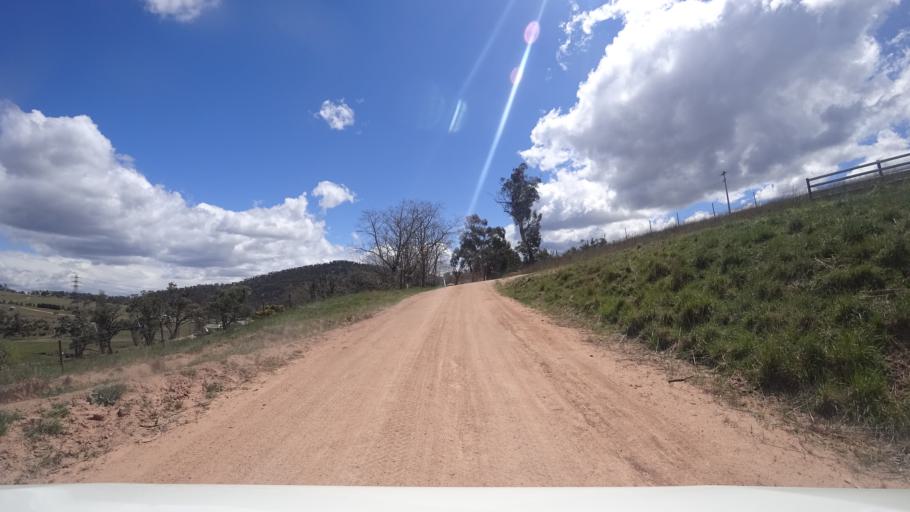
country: AU
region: New South Wales
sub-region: Oberon
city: Oberon
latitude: -33.5654
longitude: 149.9412
